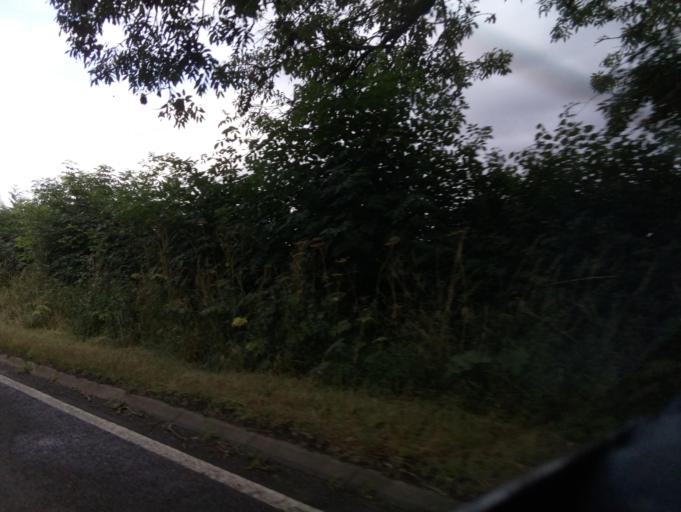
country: GB
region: England
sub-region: Warwickshire
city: Long Itchington
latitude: 52.2716
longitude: -1.3687
